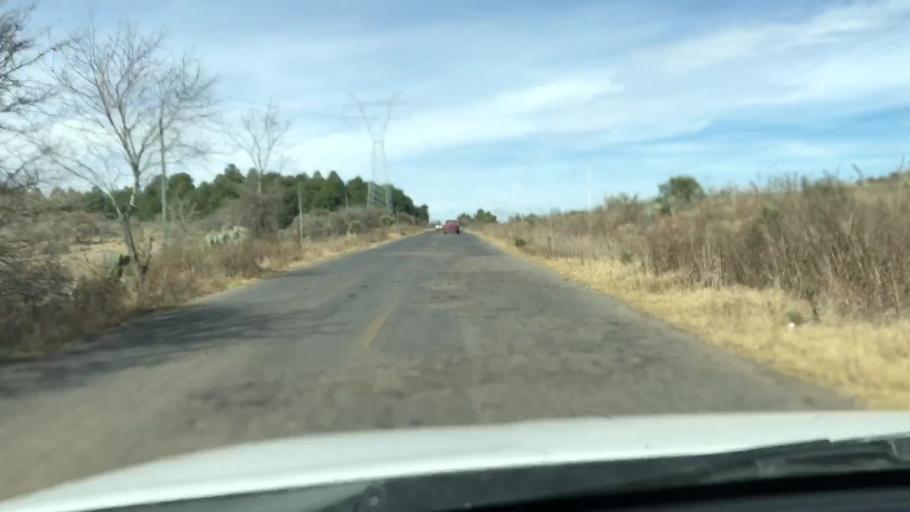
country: MX
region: Jalisco
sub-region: Amacueca
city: Tepec
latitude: 20.1026
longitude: -103.7183
